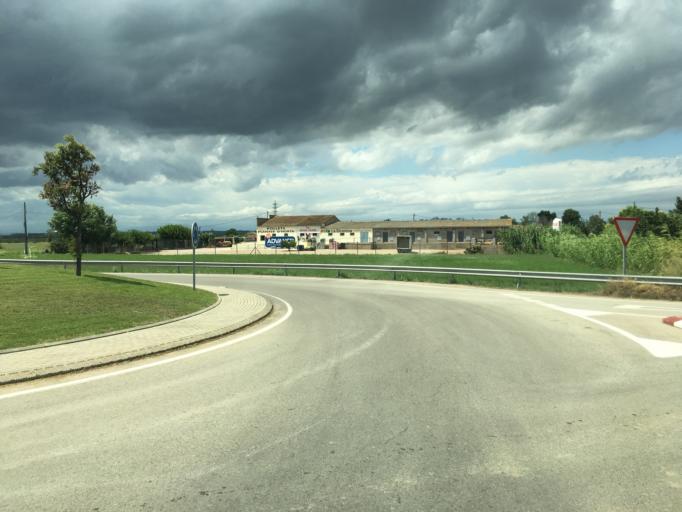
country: ES
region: Catalonia
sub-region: Provincia de Girona
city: Ulla
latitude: 42.0499
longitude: 3.1047
